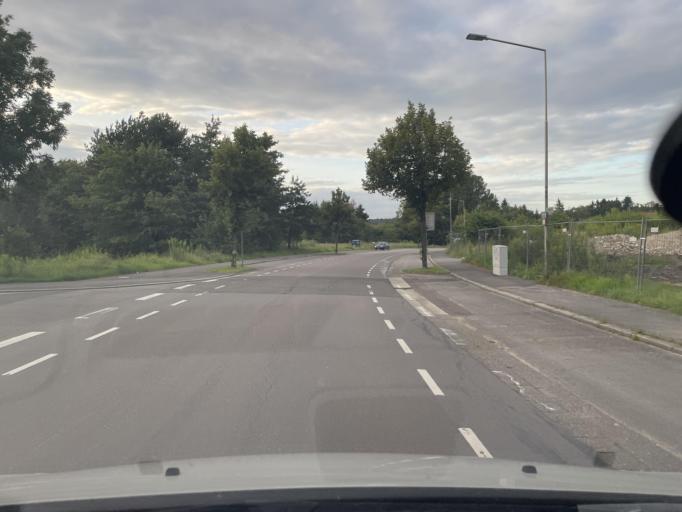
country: DE
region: Saarland
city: Sankt Ingbert
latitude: 49.2812
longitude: 7.1567
